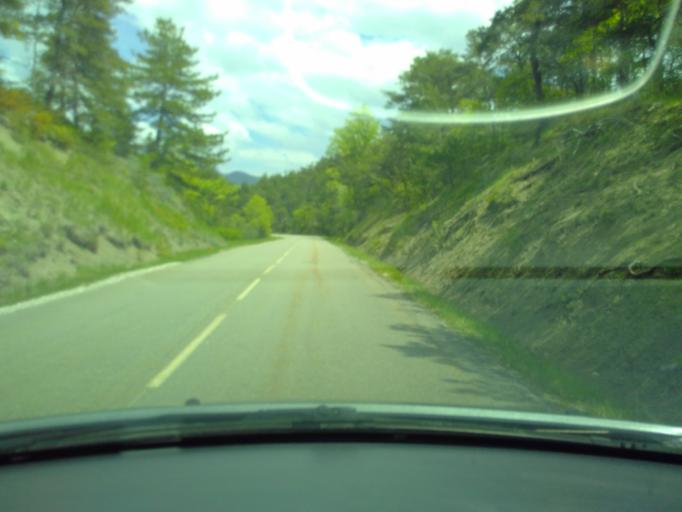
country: FR
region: Rhone-Alpes
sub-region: Departement de la Drome
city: Die
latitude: 44.6462
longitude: 5.4423
